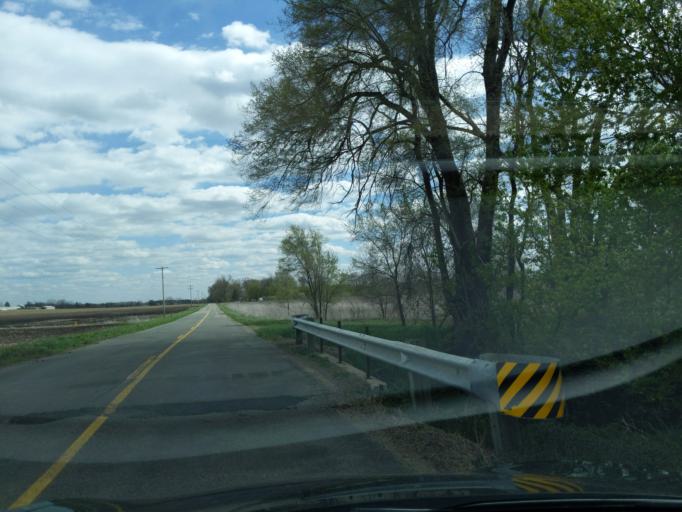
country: US
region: Michigan
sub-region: Ingham County
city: Mason
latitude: 42.5323
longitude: -84.5422
